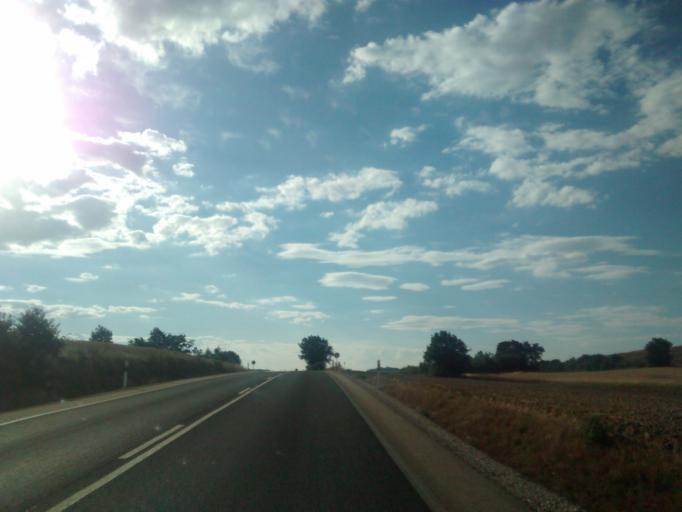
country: ES
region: Castille and Leon
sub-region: Provincia de Burgos
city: Basconcillos del Tozo
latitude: 42.6707
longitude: -3.9290
